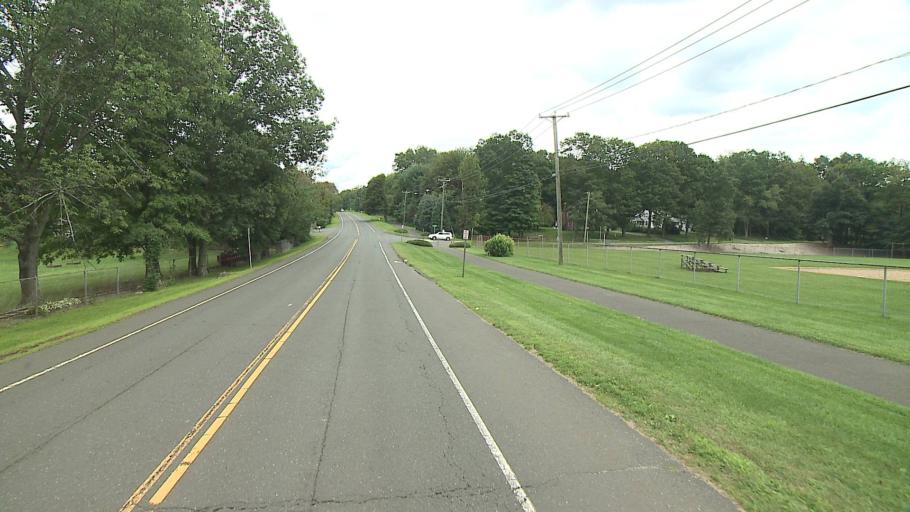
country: US
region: Connecticut
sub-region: New Haven County
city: Middlebury
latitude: 41.5253
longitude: -73.1516
